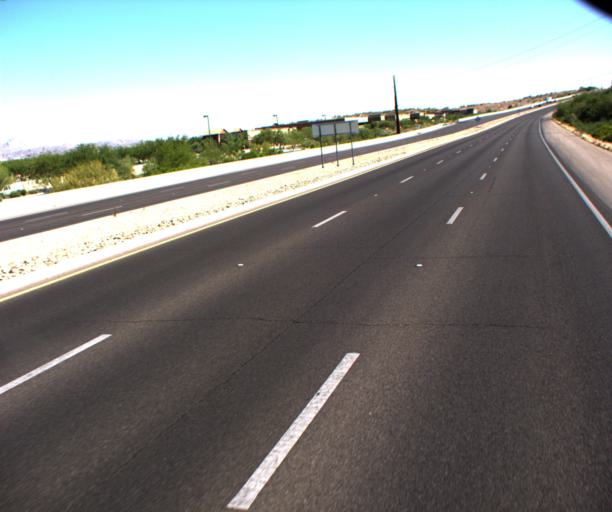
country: US
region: Arizona
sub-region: Pima County
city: Oro Valley
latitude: 32.4183
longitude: -110.9373
